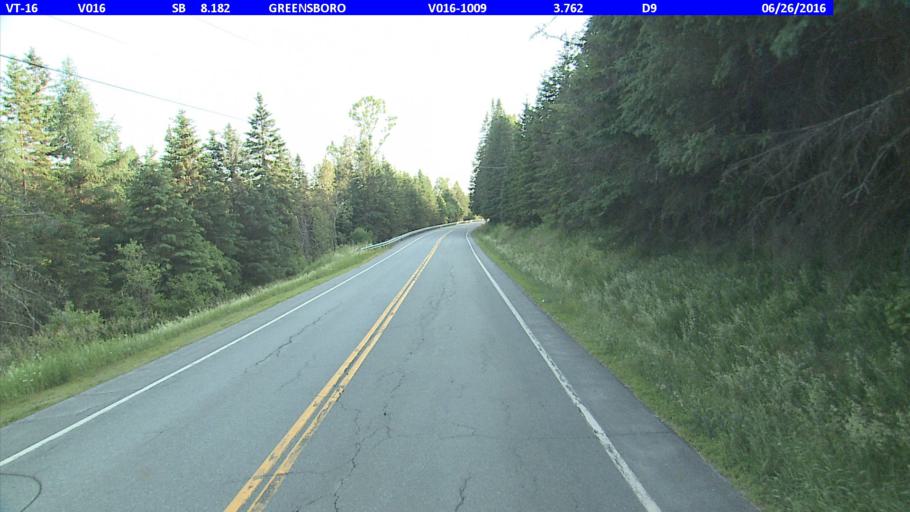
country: US
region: Vermont
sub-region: Caledonia County
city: Hardwick
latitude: 44.5919
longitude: -72.2330
